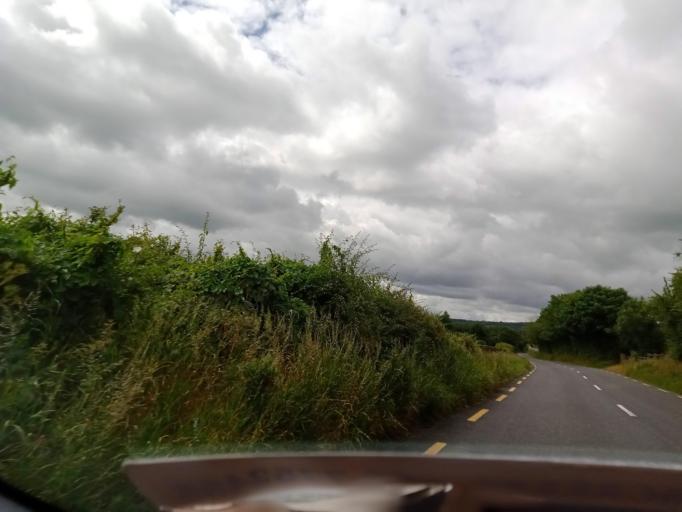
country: IE
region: Leinster
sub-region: Kilkenny
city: Thomastown
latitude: 52.4784
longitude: -7.2565
